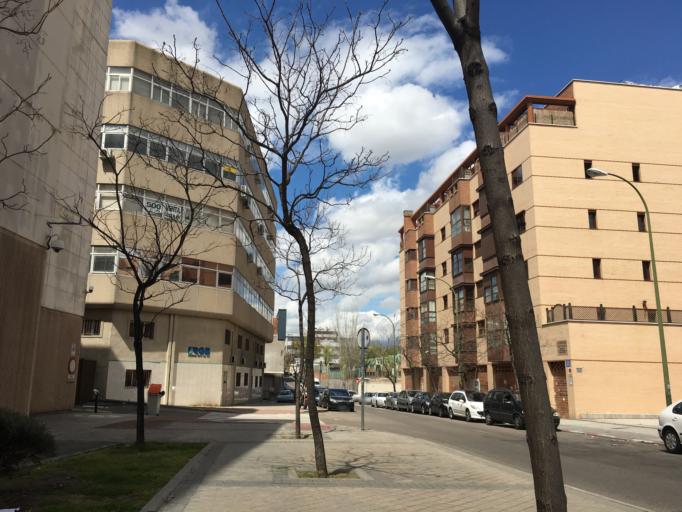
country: ES
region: Madrid
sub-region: Provincia de Madrid
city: San Blas
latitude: 40.4336
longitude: -3.6259
